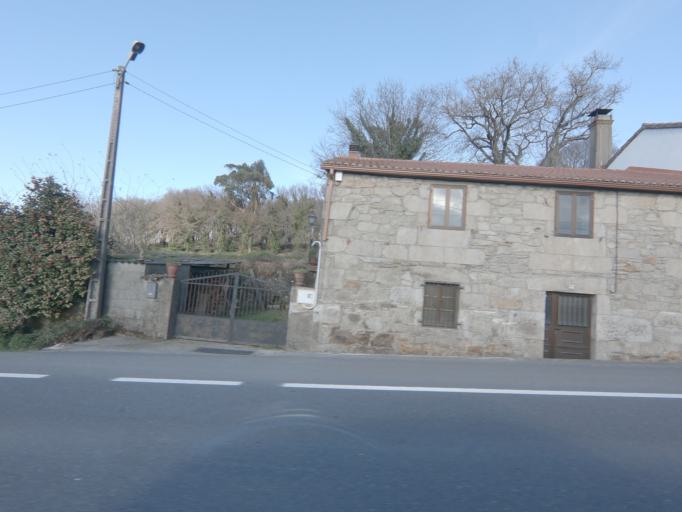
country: ES
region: Galicia
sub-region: Provincia de Pontevedra
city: Silleda
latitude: 42.7071
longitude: -8.2657
